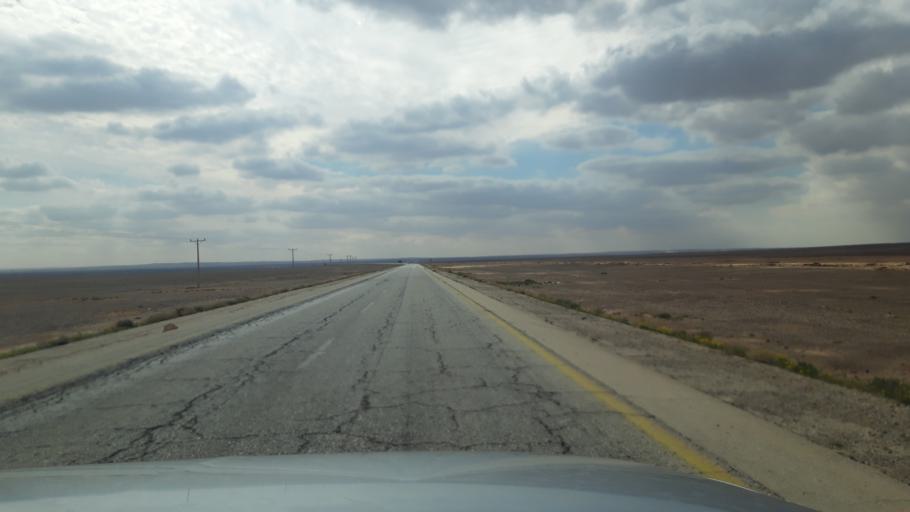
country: JO
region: Amman
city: Al Azraq ash Shamali
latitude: 31.8458
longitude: 36.6557
